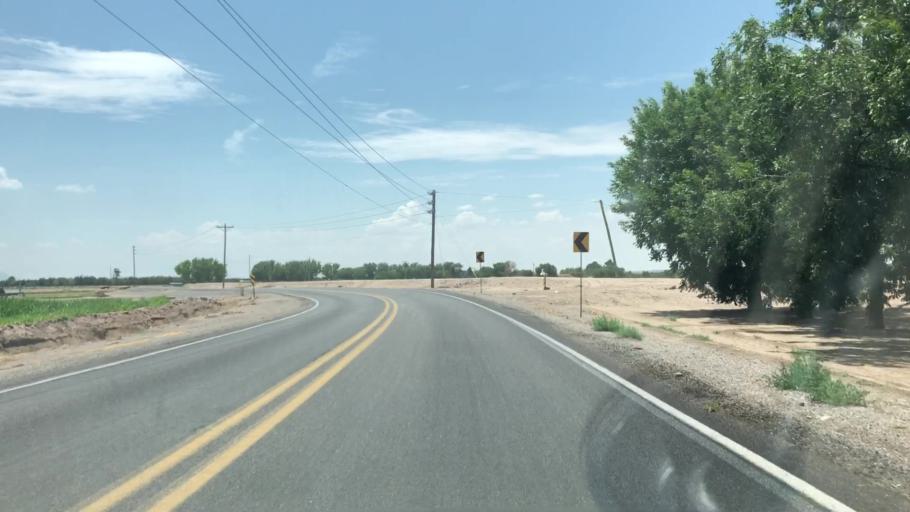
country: US
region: New Mexico
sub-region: Dona Ana County
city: Vado
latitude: 32.0942
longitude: -106.6836
